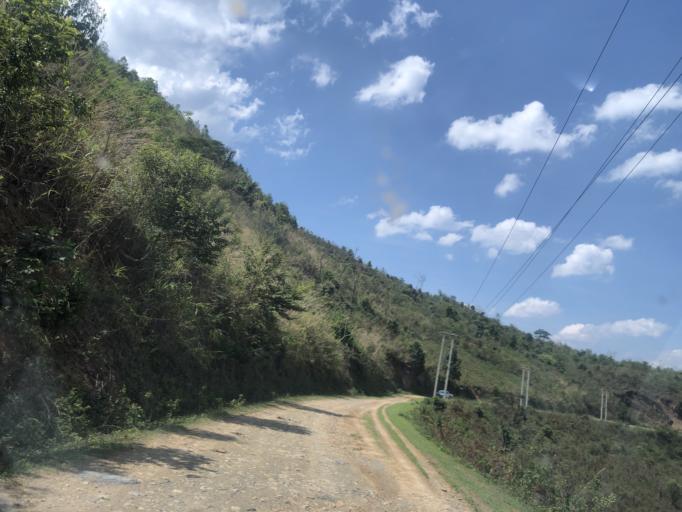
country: LA
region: Phongsali
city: Phongsali
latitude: 21.4091
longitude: 102.2397
